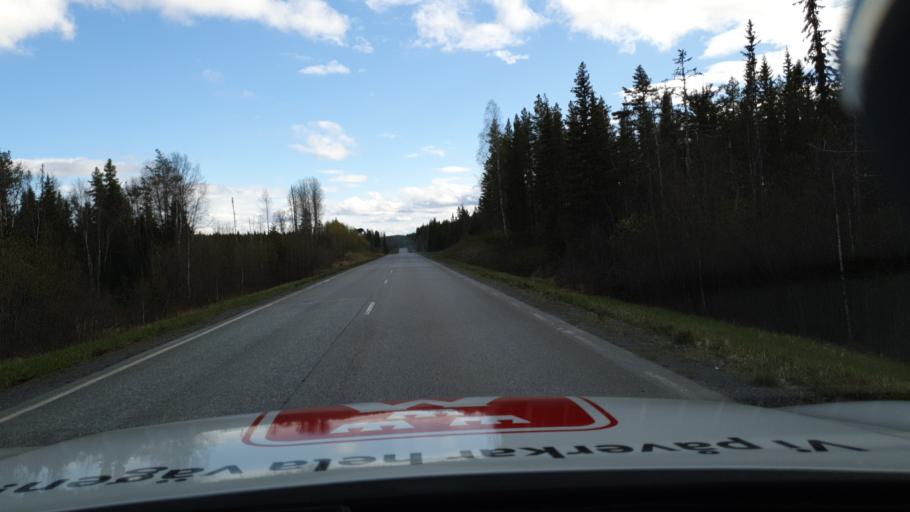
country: SE
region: Jaemtland
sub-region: Krokoms Kommun
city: Krokom
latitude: 63.2830
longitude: 14.4420
